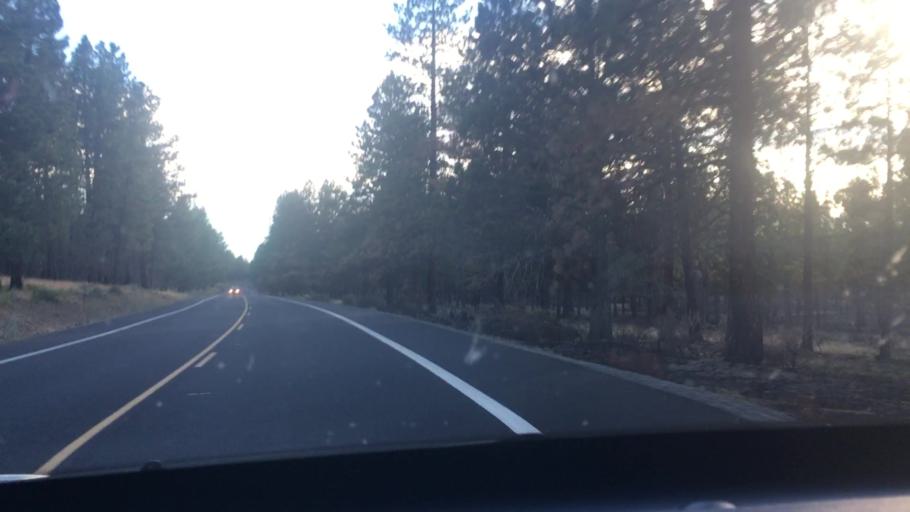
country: US
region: Oregon
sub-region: Deschutes County
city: Deschutes River Woods
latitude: 44.0486
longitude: -121.3920
